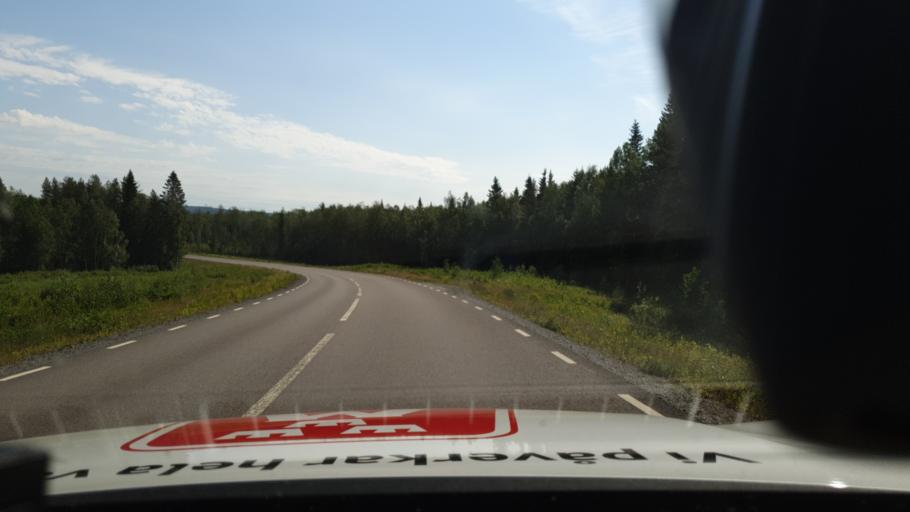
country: SE
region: Norrbotten
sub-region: Lulea Kommun
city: Sodra Sunderbyn
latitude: 65.8198
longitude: 21.9090
